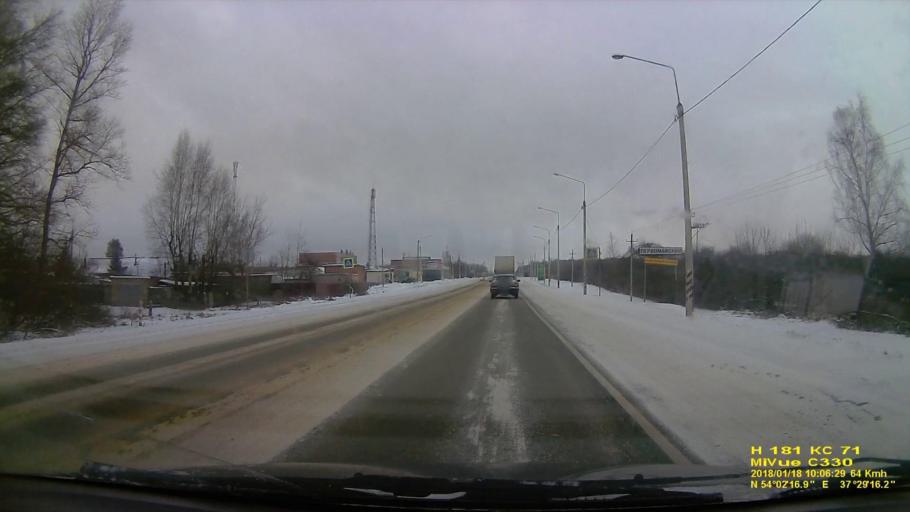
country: RU
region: Tula
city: Pervomayskiy
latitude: 54.0377
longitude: 37.4880
